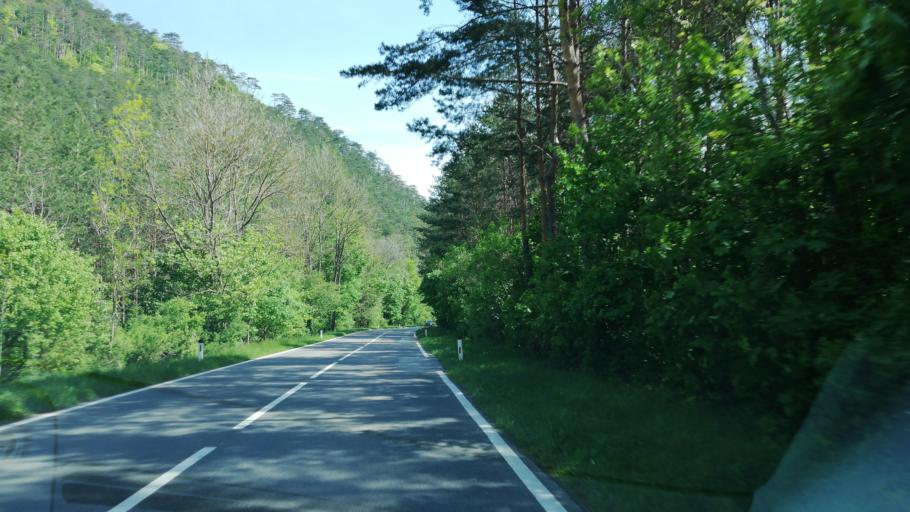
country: AT
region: Lower Austria
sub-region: Politischer Bezirk Modling
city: Gaaden
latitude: 48.0159
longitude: 16.1743
